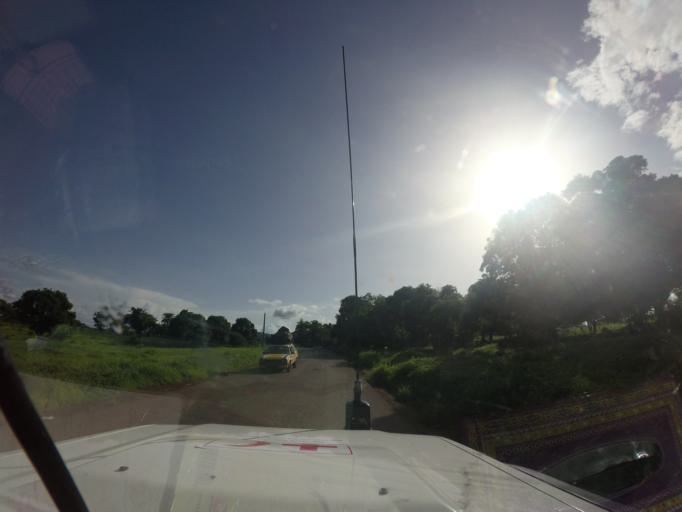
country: GN
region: Kindia
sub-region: Kindia
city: Kindia
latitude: 10.0725
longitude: -12.5974
